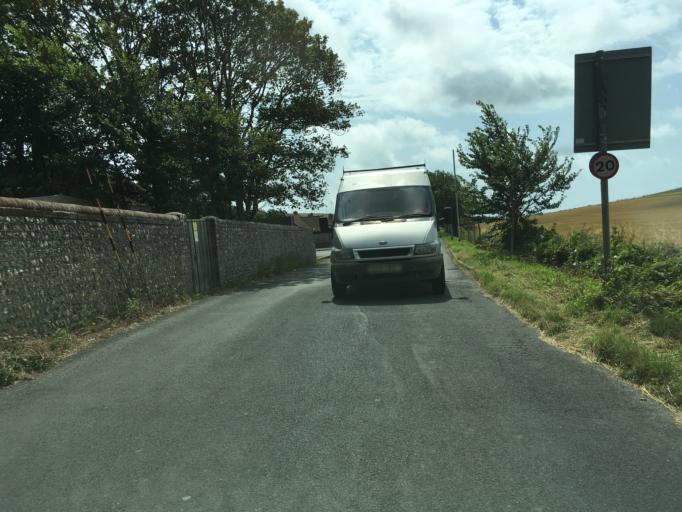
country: GB
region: England
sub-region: Brighton and Hove
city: Rottingdean
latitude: 50.8150
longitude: -0.0746
